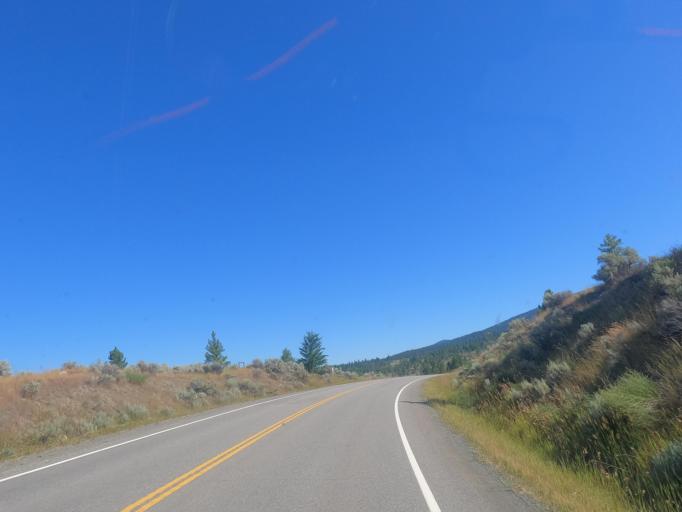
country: CA
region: British Columbia
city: Merritt
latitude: 50.1935
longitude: -120.8519
